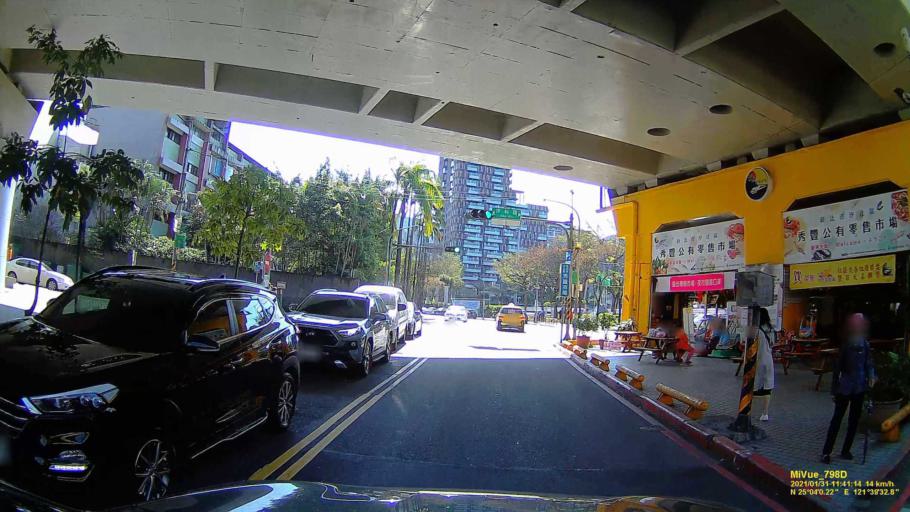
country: TW
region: Taiwan
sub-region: Keelung
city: Keelung
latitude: 25.0666
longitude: 121.6591
